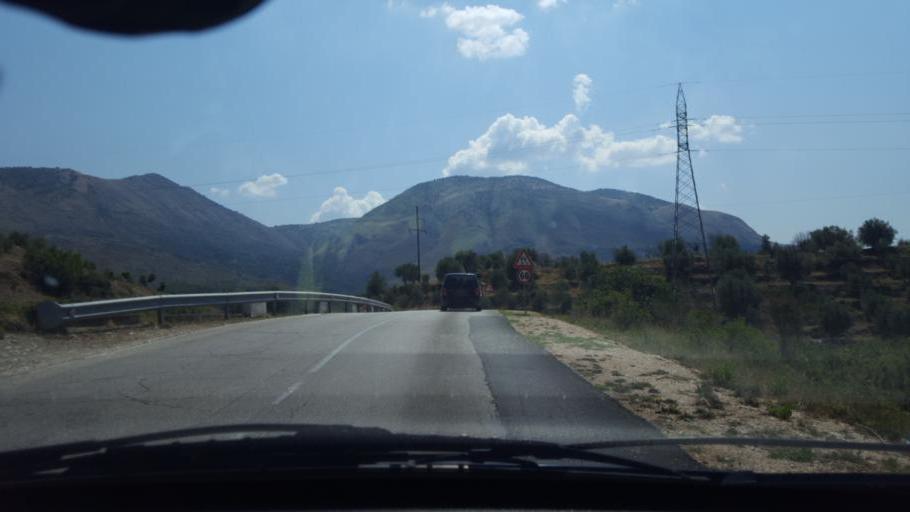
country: AL
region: Vlore
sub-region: Rrethi i Delvines
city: Mesopotam
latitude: 39.9110
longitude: 20.1160
